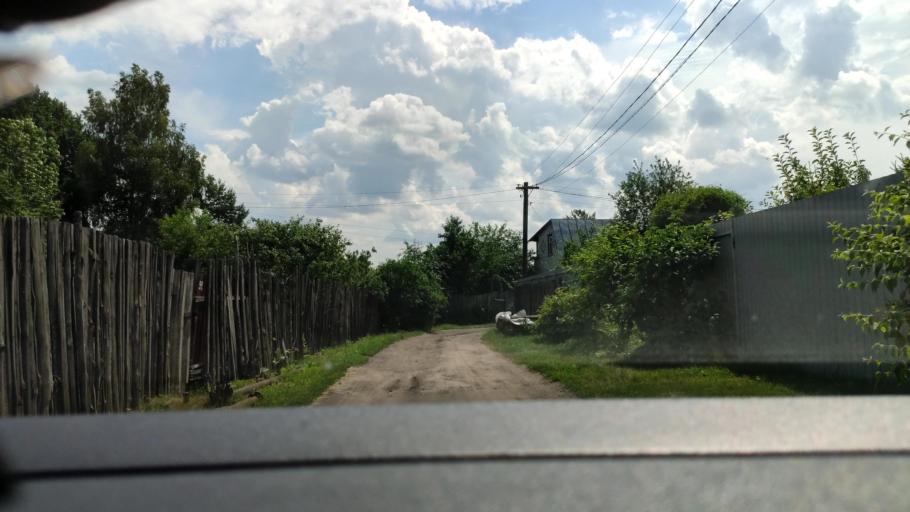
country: RU
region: Voronezj
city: Maslovka
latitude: 51.6087
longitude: 39.2876
